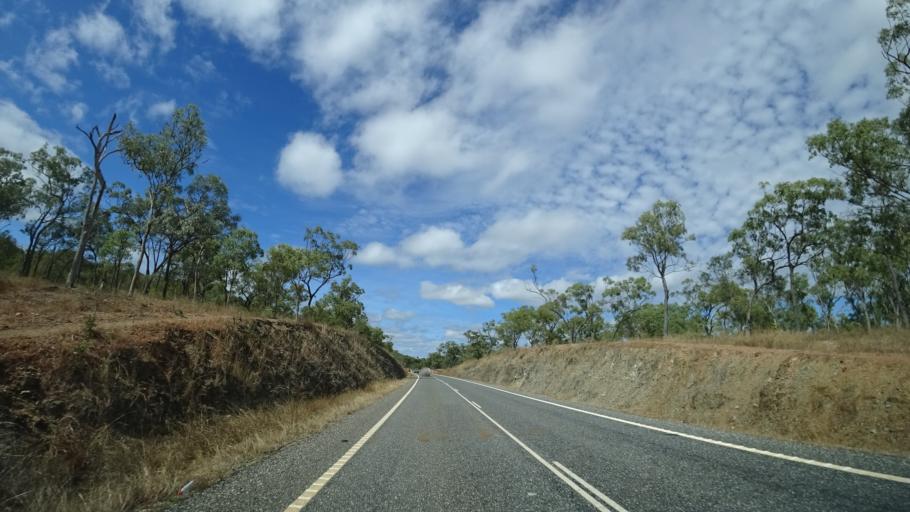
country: AU
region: Queensland
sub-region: Cairns
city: Port Douglas
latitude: -16.3321
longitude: 144.7221
